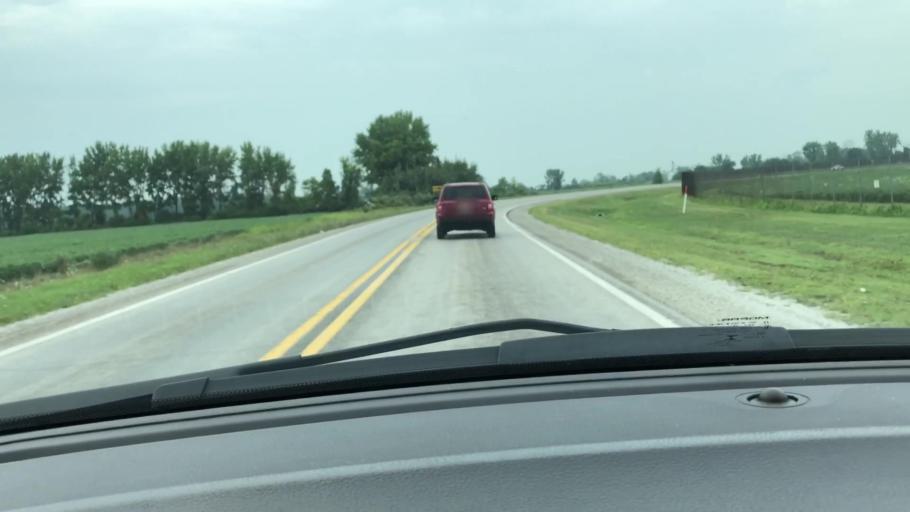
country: US
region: Michigan
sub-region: Saginaw County
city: Freeland
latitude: 43.5369
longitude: -84.0952
